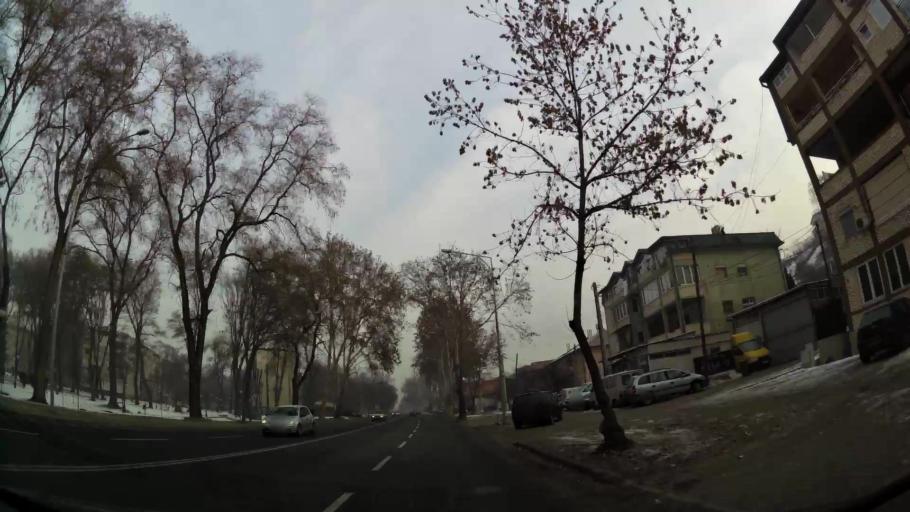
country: MK
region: Cair
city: Cair
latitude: 42.0150
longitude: 21.4464
